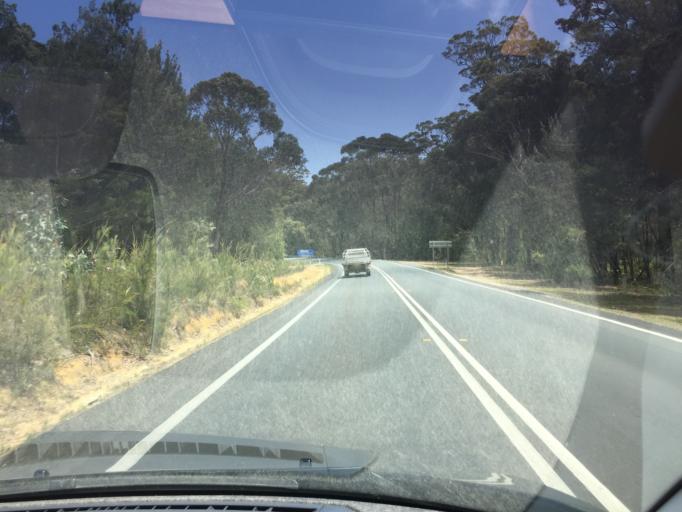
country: AU
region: New South Wales
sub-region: Bega Valley
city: Merimbula
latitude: -36.8665
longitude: 149.9031
